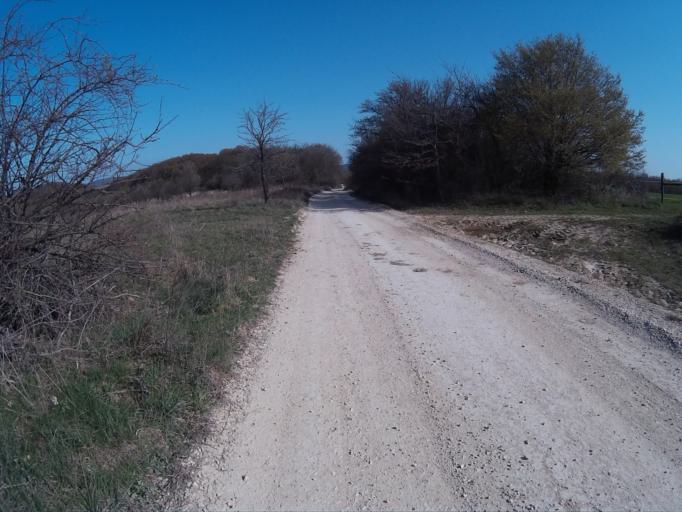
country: HU
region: Veszprem
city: Herend
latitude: 47.2019
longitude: 17.7898
